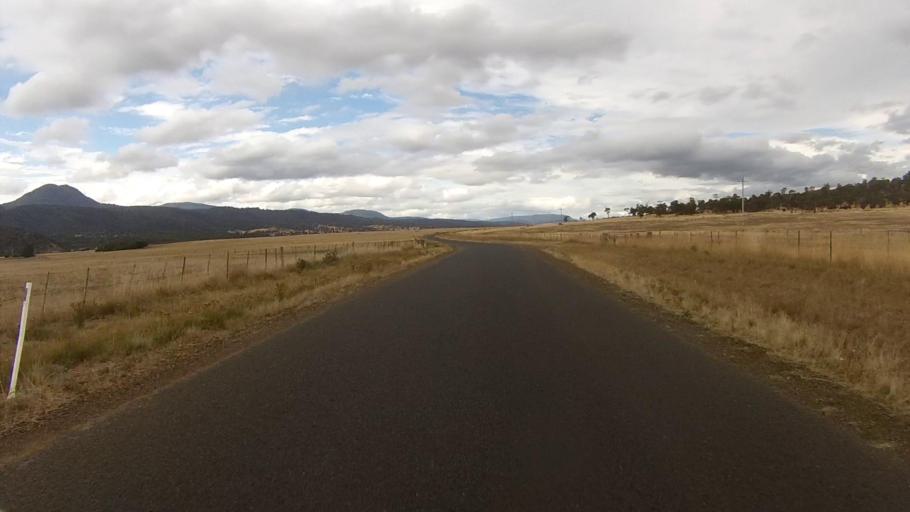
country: AU
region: Tasmania
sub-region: Northern Midlands
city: Evandale
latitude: -41.8266
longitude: 147.7911
